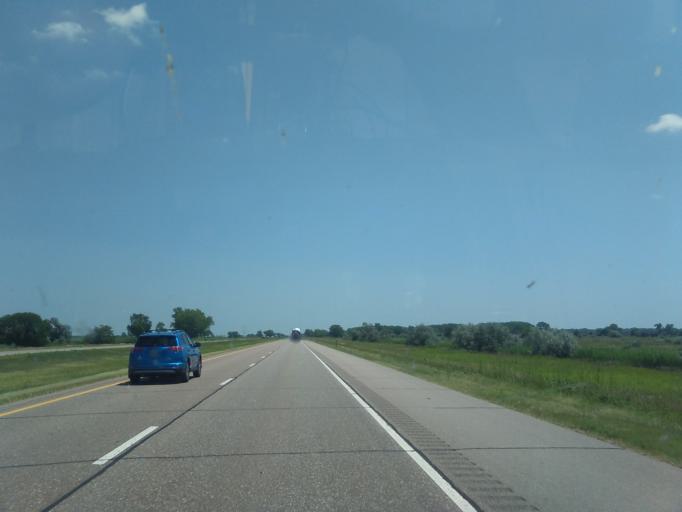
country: US
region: Nebraska
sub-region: Dawson County
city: Cozad
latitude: 40.8717
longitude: -100.0503
